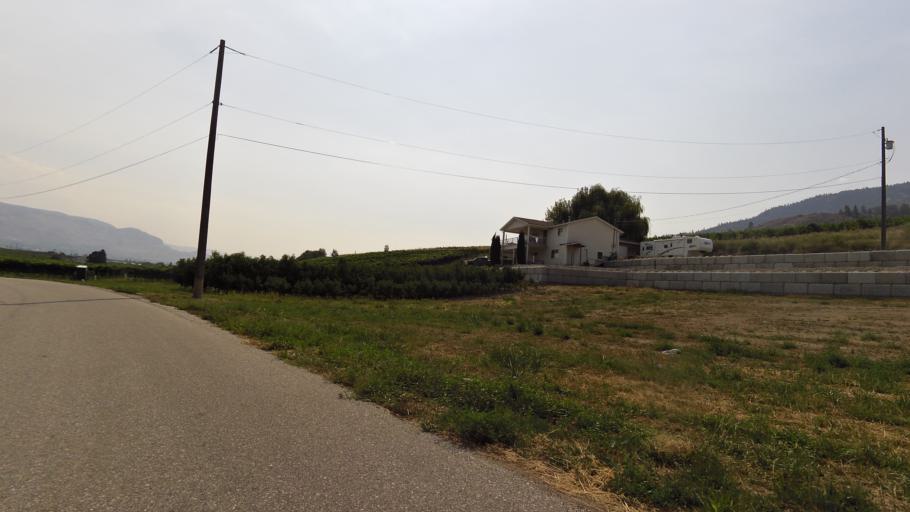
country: CA
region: British Columbia
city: Osoyoos
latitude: 49.0525
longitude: -119.5087
